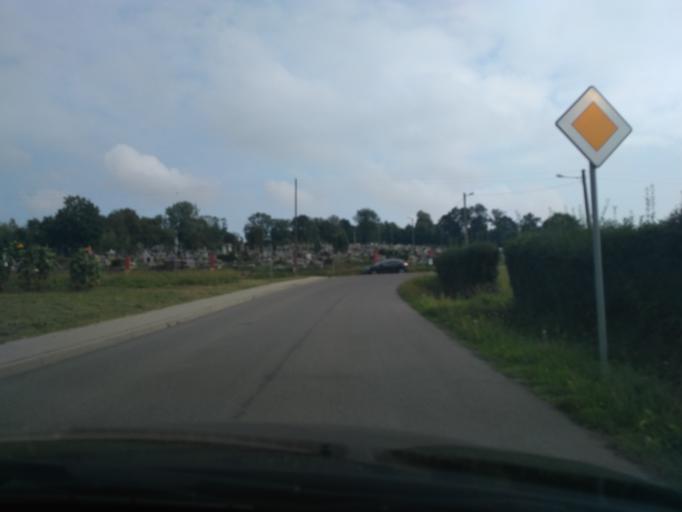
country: PL
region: Subcarpathian Voivodeship
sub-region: Powiat strzyzowski
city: Czudec
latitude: 49.9455
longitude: 21.8414
